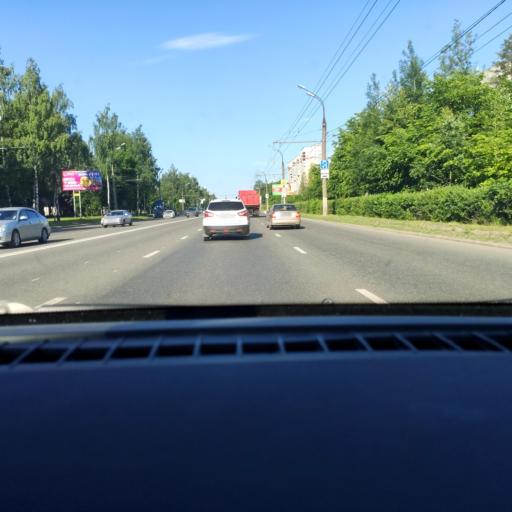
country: RU
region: Udmurtiya
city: Izhevsk
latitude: 56.8894
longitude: 53.2502
